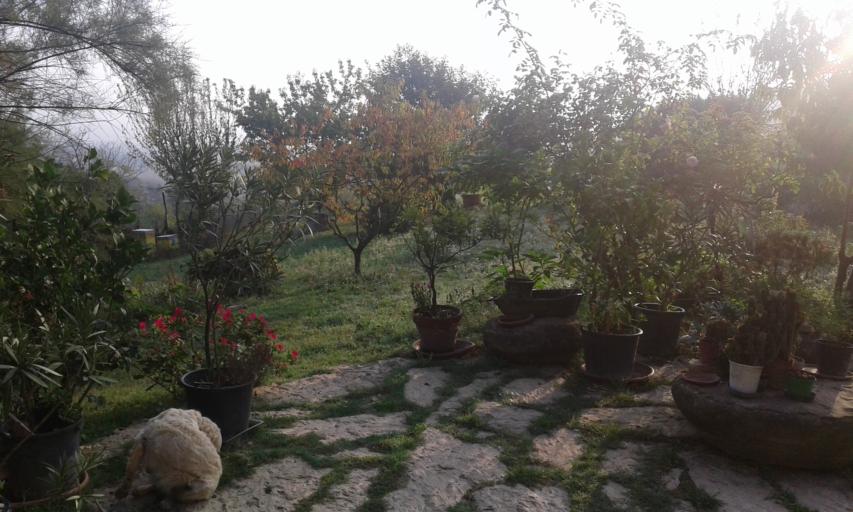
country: IT
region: Piedmont
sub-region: Provincia di Asti
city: Monastero Bormida
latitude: 44.6415
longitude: 8.3302
